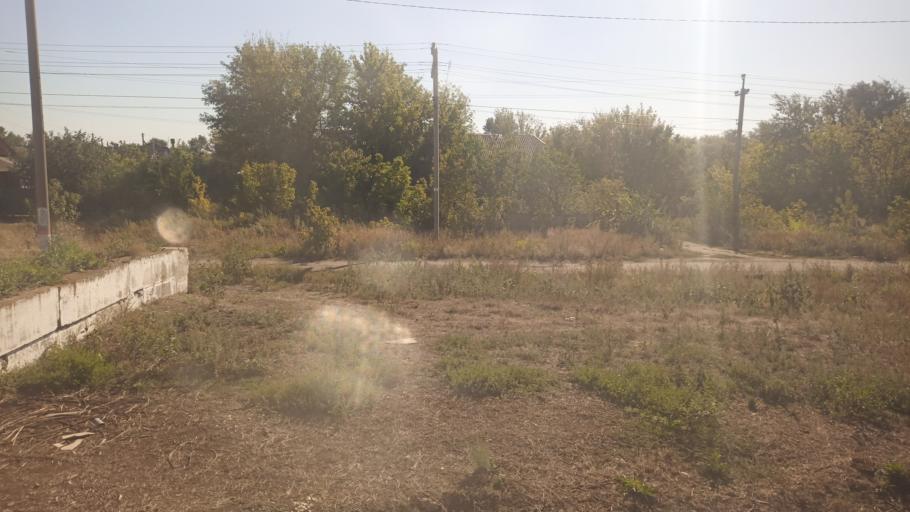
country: RU
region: Saratov
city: Pushkino
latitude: 51.2358
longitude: 46.9796
